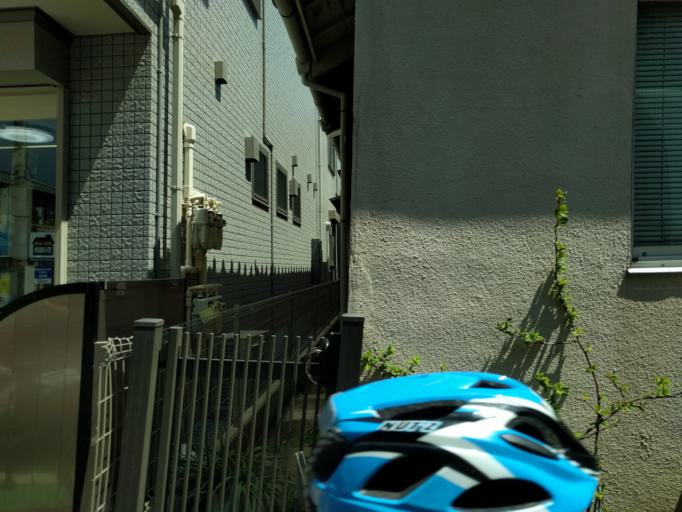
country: JP
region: Tokyo
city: Chofugaoka
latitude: 35.6453
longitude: 139.6086
